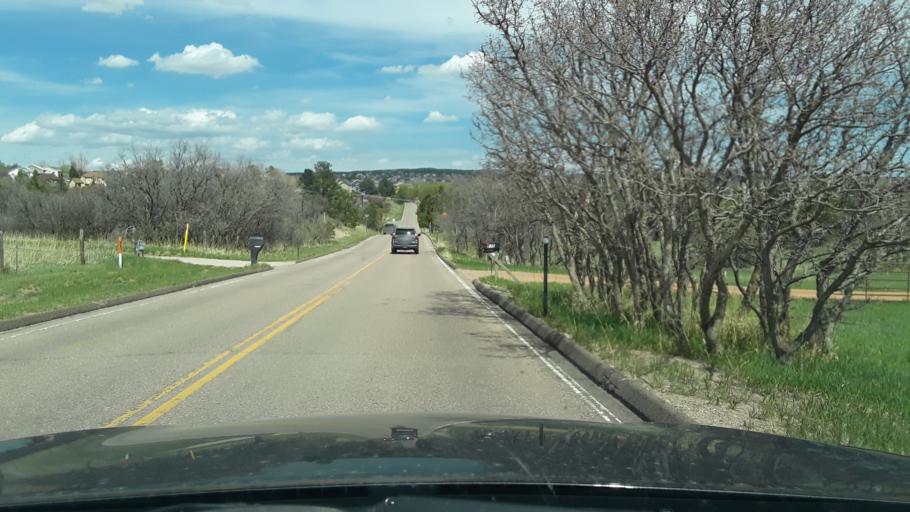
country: US
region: Colorado
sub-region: El Paso County
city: Monument
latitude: 39.0823
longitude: -104.8792
